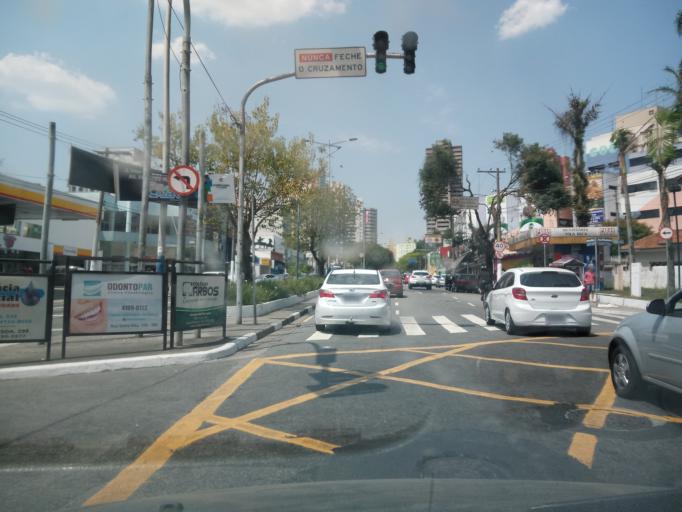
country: BR
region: Sao Paulo
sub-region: Sao Bernardo Do Campo
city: Sao Bernardo do Campo
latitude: -23.7057
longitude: -46.5507
